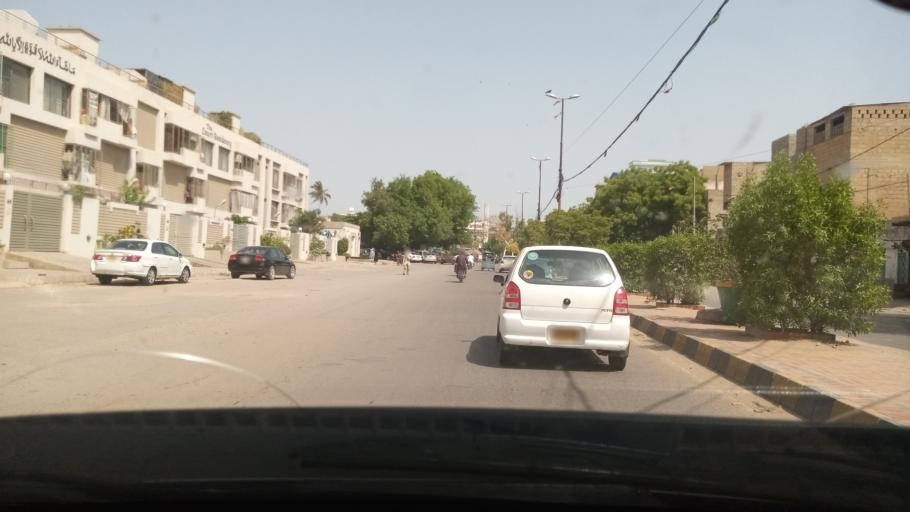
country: PK
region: Sindh
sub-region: Karachi District
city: Karachi
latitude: 24.8740
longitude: 67.0473
